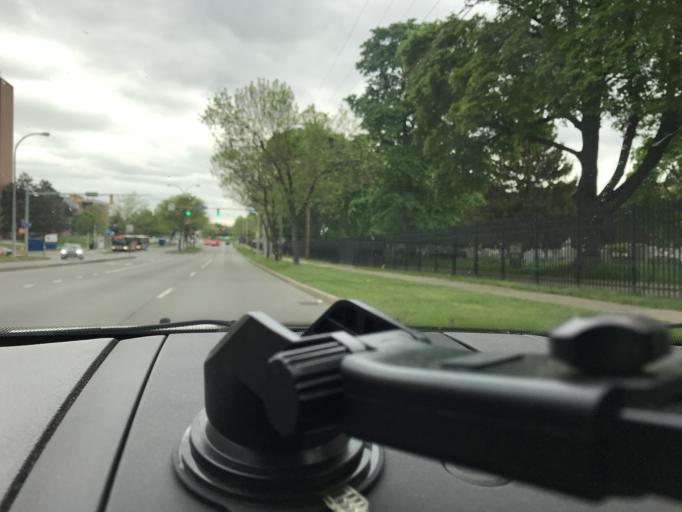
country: US
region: New York
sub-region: Monroe County
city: Rochester
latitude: 43.1247
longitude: -77.6207
